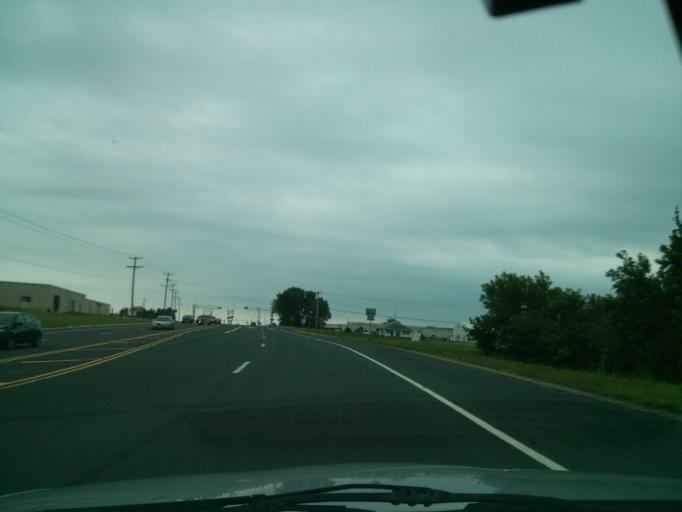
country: US
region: Wisconsin
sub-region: Saint Croix County
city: North Hudson
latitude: 44.9916
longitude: -92.6805
